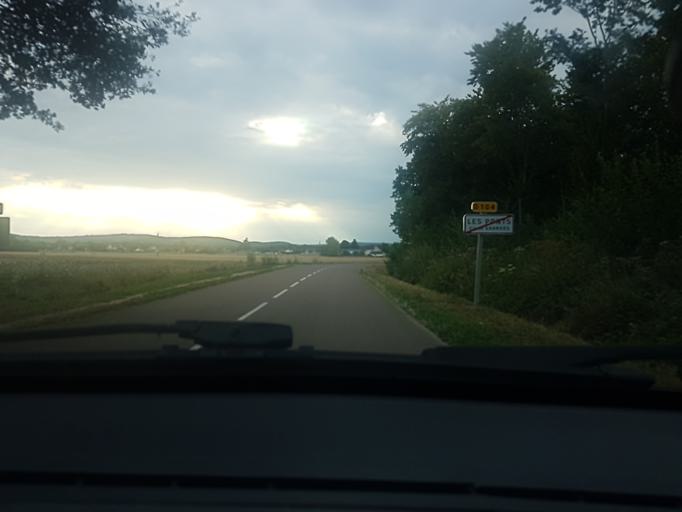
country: FR
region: Bourgogne
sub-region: Departement de Saone-et-Loire
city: Buxy
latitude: 46.7260
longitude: 4.7578
